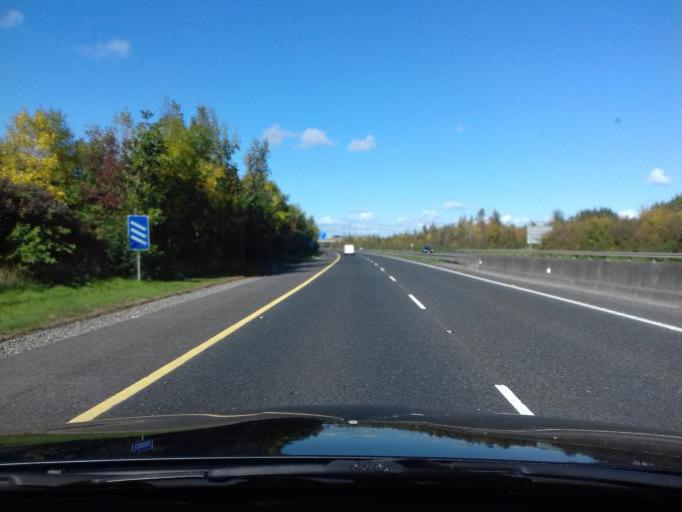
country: IE
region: Leinster
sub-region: An Mhi
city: Ashbourne
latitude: 53.4815
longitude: -6.3747
